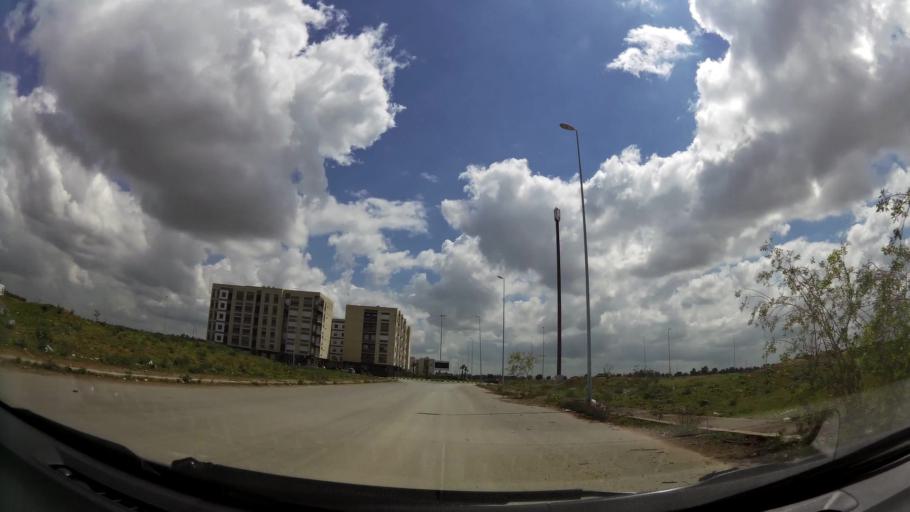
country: MA
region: Chaouia-Ouardigha
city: Nouaseur
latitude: 33.3899
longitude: -7.5610
